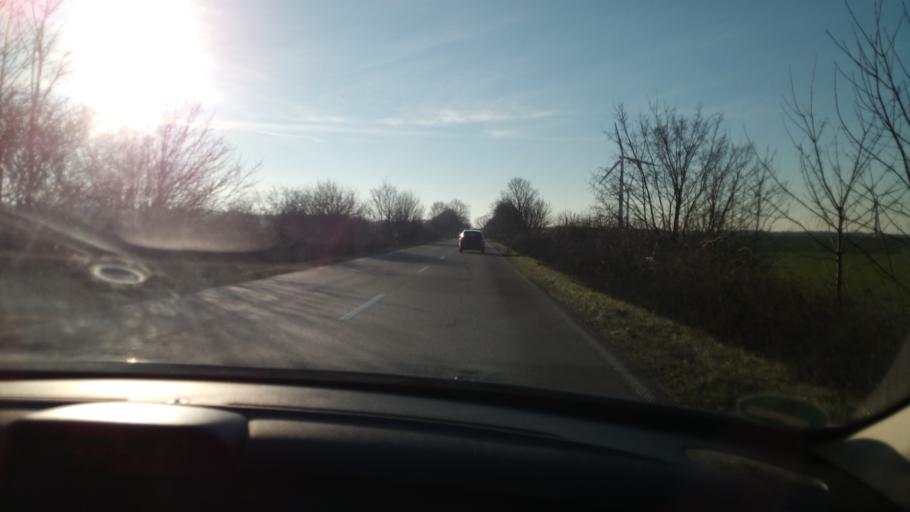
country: DE
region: Schleswig-Holstein
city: Basedow
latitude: 53.4170
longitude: 10.5753
